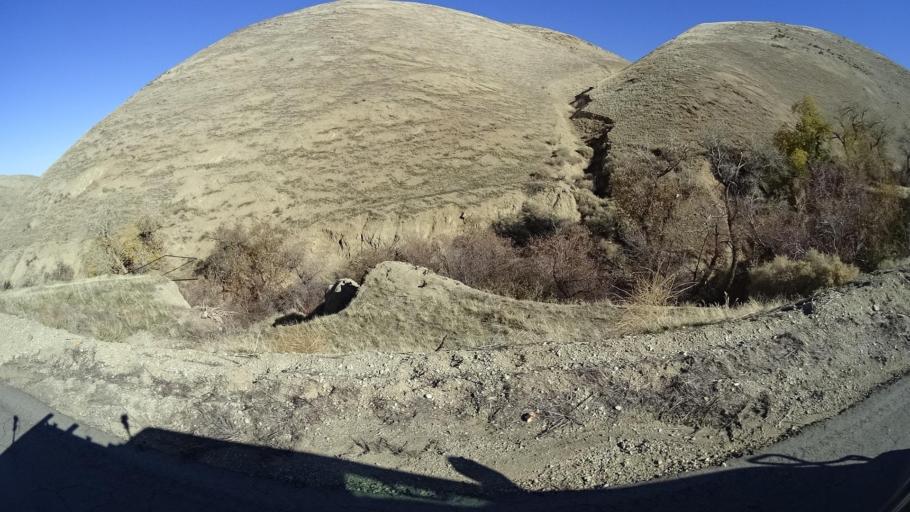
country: US
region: California
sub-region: Kern County
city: Maricopa
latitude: 34.9682
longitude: -119.4141
